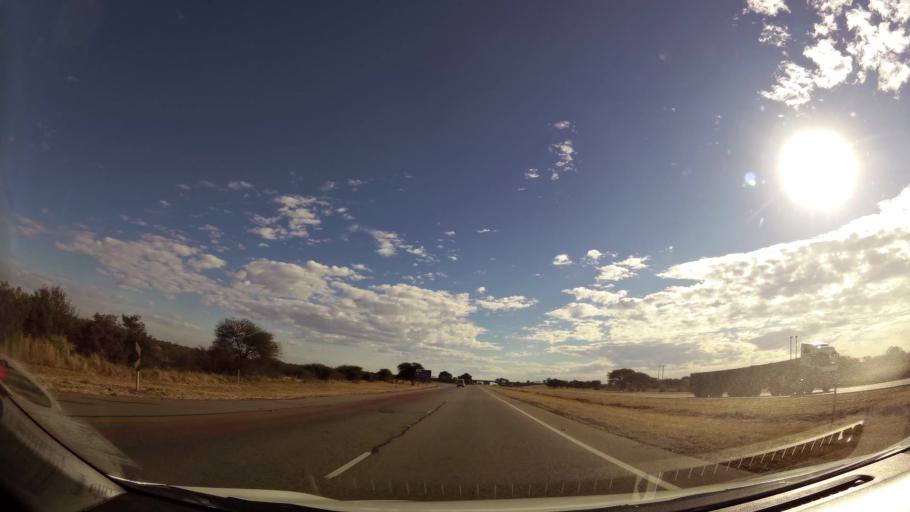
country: ZA
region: North-West
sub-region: Bojanala Platinum District Municipality
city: Makapanstad
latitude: -25.2892
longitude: 28.2982
